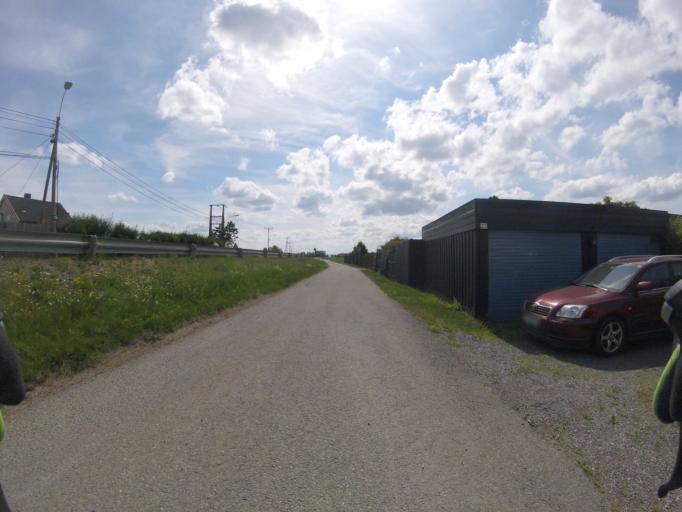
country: NO
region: Akershus
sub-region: Skedsmo
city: Lillestrom
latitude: 59.9819
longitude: 11.0518
